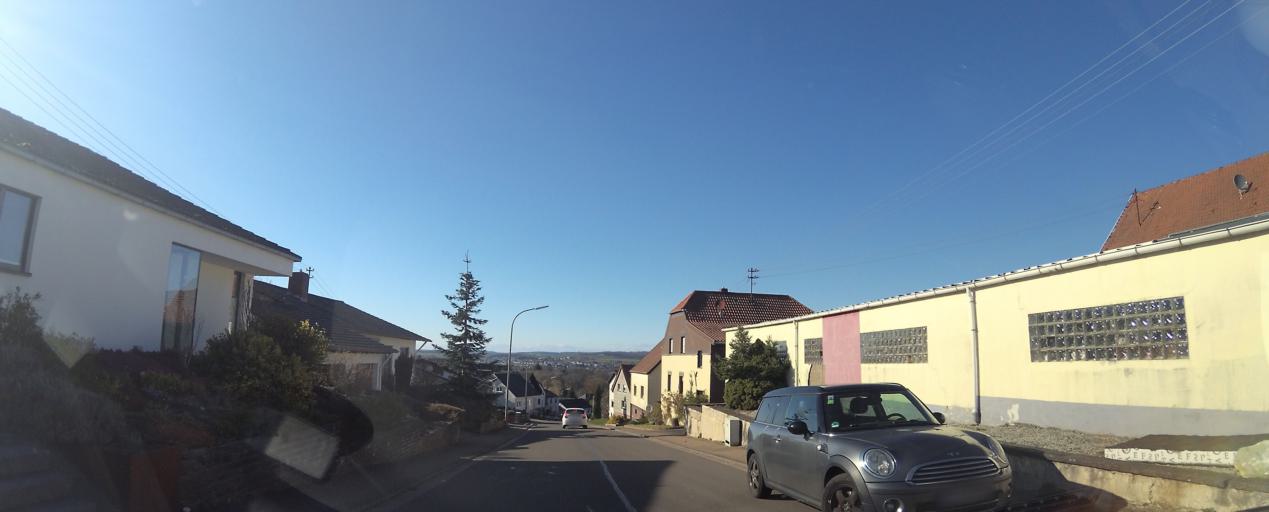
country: DE
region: Saarland
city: Riegelsberg
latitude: 49.3176
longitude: 6.9503
